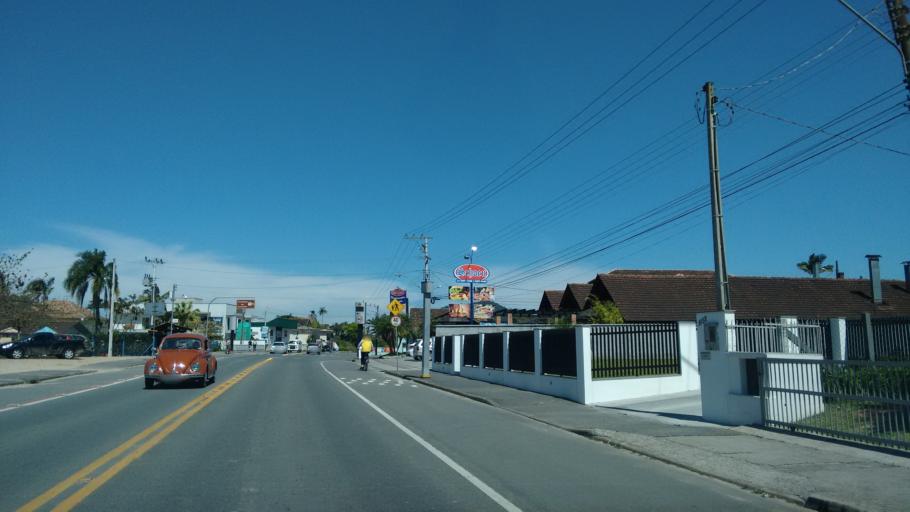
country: BR
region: Santa Catarina
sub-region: Pomerode
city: Pomerode
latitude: -26.7461
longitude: -49.1741
